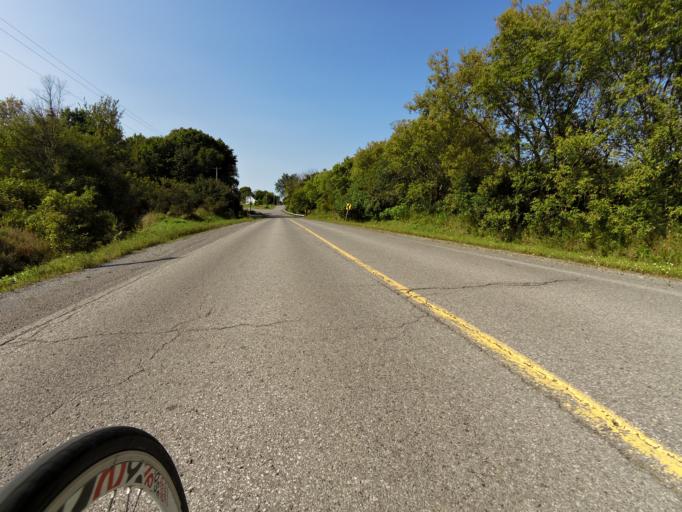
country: CA
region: Ontario
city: Carleton Place
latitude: 45.3546
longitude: -76.1178
